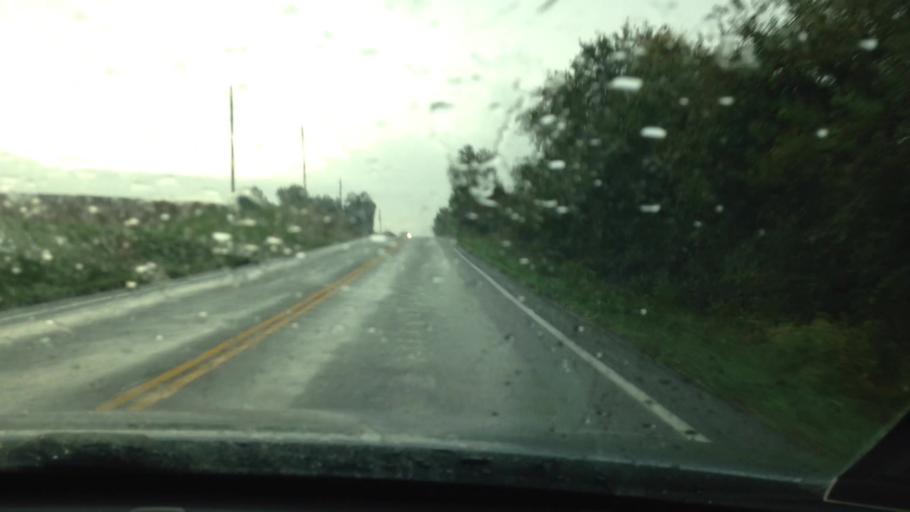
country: US
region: Missouri
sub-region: Platte County
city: Weston
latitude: 39.3974
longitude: -94.8592
